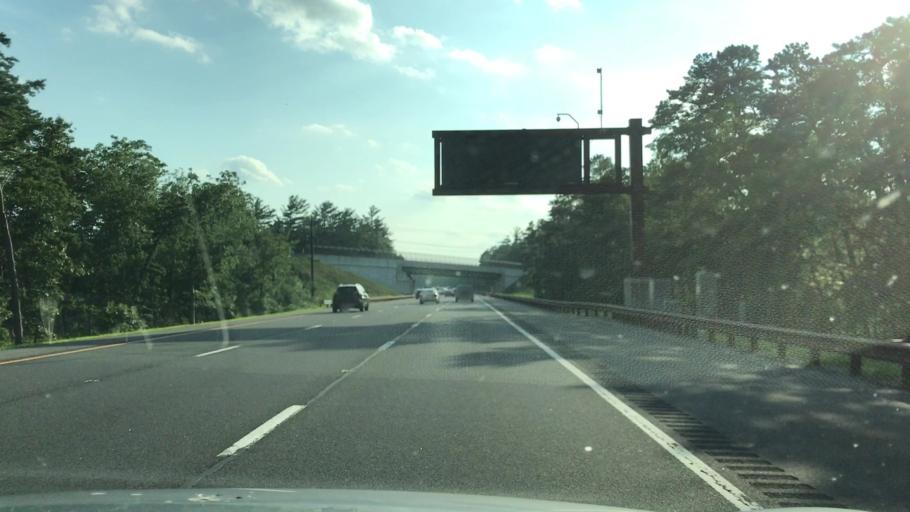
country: US
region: New Jersey
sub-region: Ocean County
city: Tuckerton
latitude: 39.6188
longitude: -74.4116
